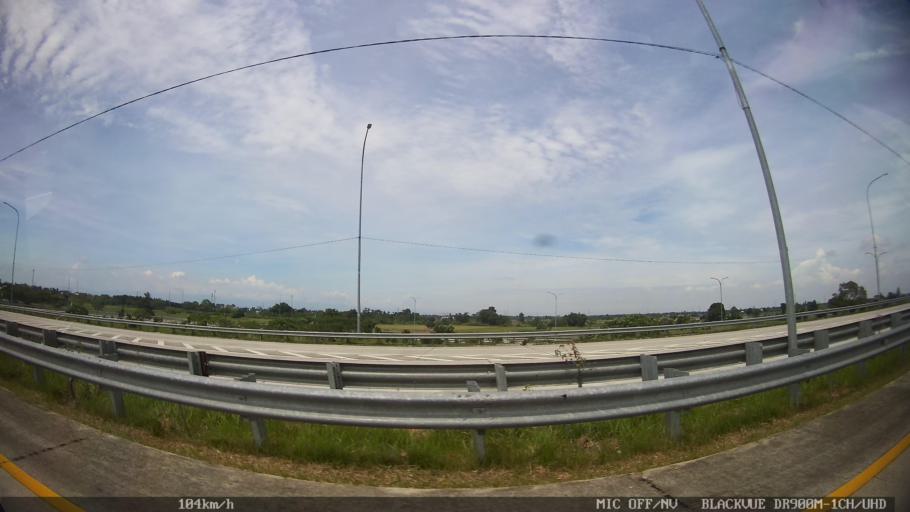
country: ID
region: North Sumatra
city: Percut
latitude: 3.5625
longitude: 98.8503
